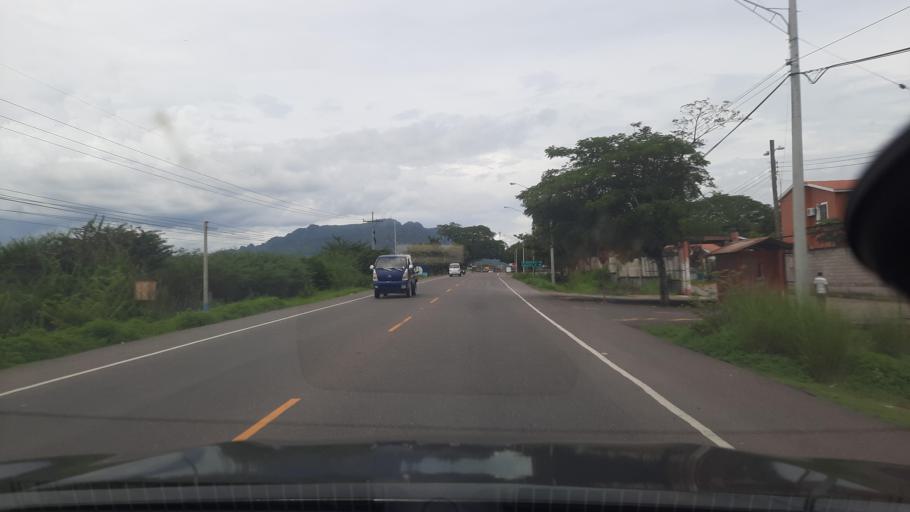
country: HN
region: Valle
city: Jicaro Galan
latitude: 13.5321
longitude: -87.4459
